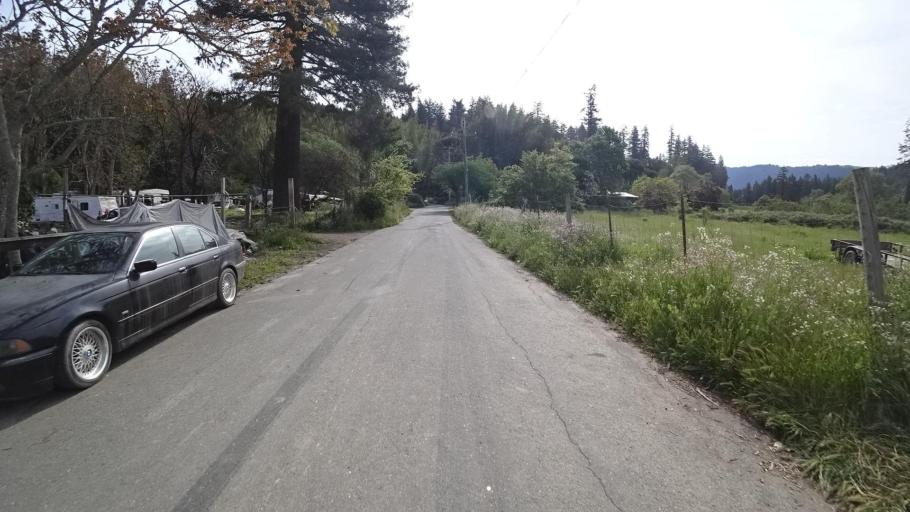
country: US
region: California
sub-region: Humboldt County
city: Redway
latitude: 40.2075
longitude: -123.7879
